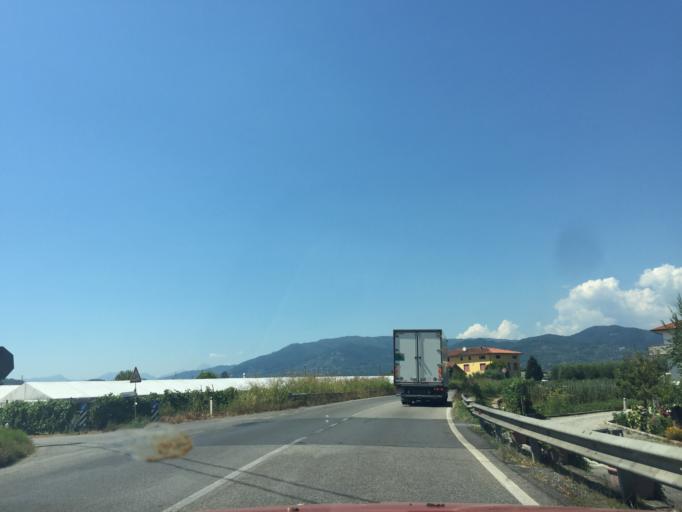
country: IT
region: Tuscany
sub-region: Provincia di Pistoia
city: Chiesina Uzzanese
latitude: 43.8546
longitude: 10.7046
